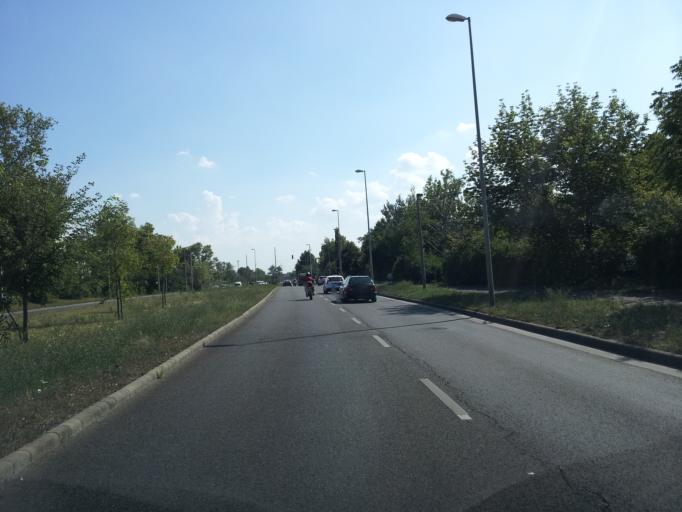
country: HU
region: Budapest
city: Budapest XI. keruelet
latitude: 47.4568
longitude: 19.0466
